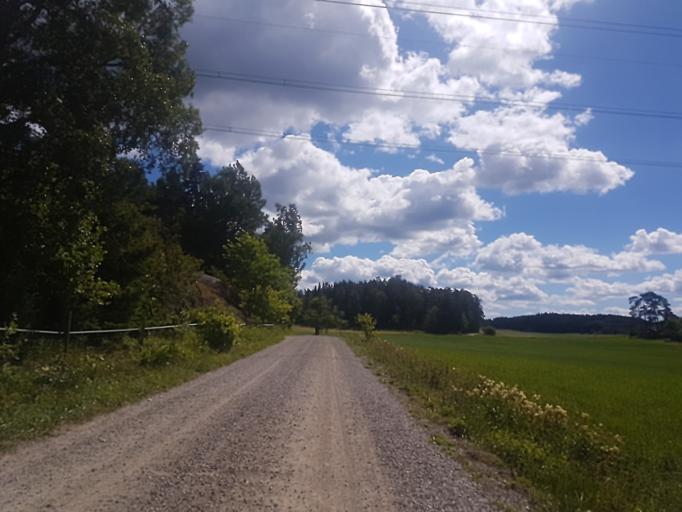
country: SE
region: Stockholm
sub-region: Sodertalje Kommun
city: Molnbo
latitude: 59.0047
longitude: 17.3760
